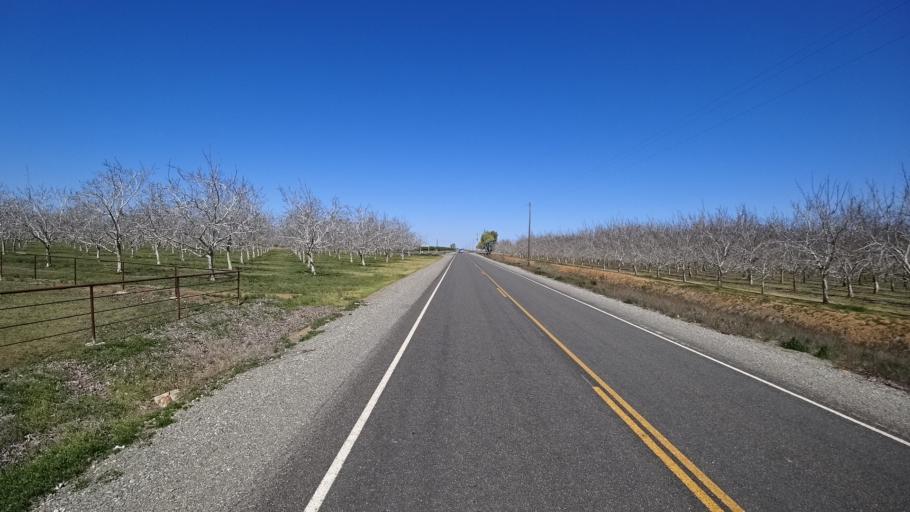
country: US
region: California
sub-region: Glenn County
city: Willows
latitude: 39.4496
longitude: -122.2488
